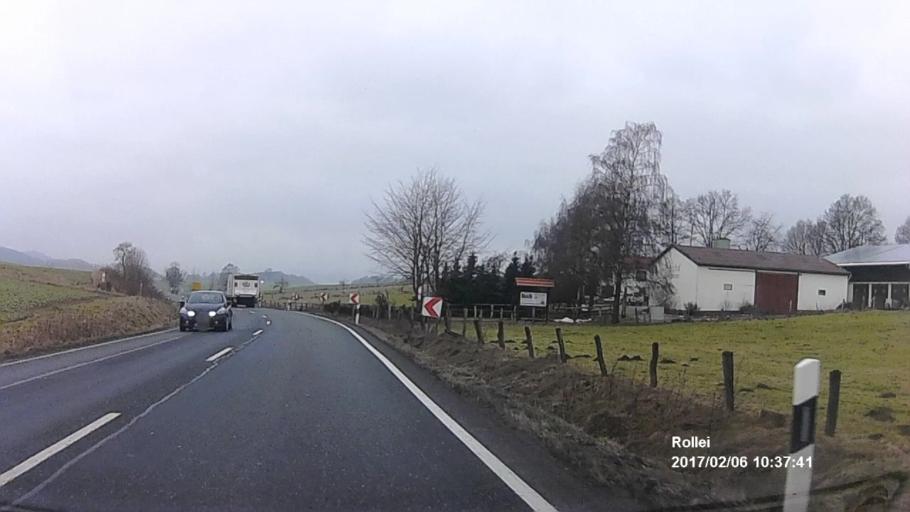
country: DE
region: Lower Saxony
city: Osterode am Harz
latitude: 51.7271
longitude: 10.2226
